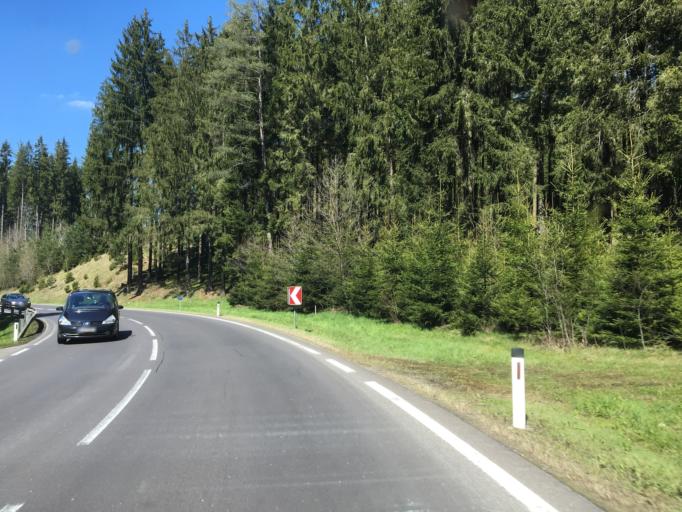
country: AT
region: Upper Austria
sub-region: Politischer Bezirk Urfahr-Umgebung
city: Bad Leonfelden
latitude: 48.4903
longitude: 14.2979
